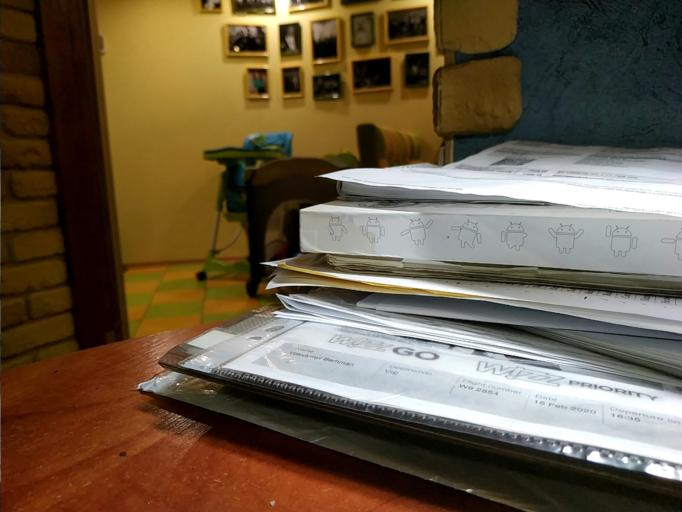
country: RU
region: Arkhangelskaya
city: Voloshka
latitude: 61.1678
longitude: 39.5189
